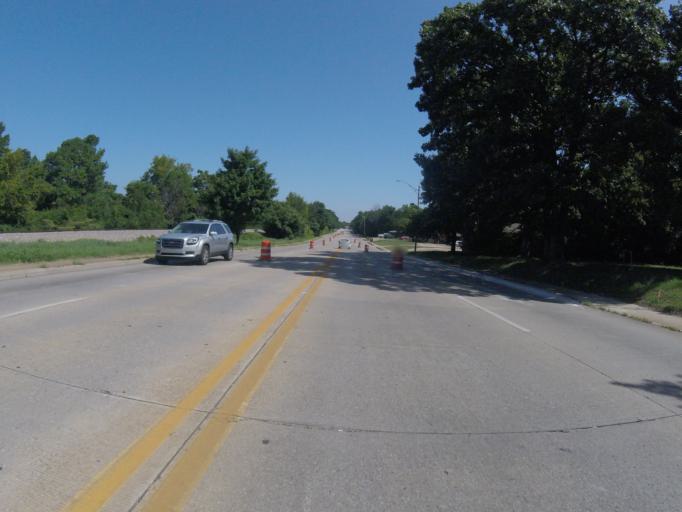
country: US
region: Arkansas
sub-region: Washington County
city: Fayetteville
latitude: 36.0887
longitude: -94.1622
